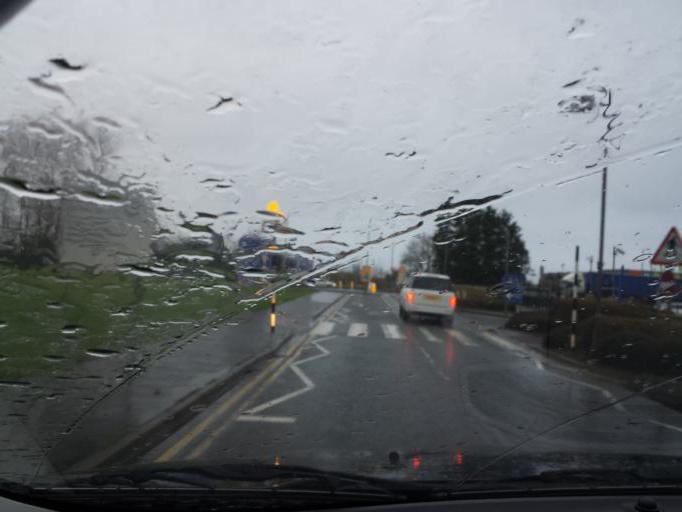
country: GB
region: Northern Ireland
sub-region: Antrim Borough
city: Antrim
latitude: 54.6634
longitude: -6.2183
